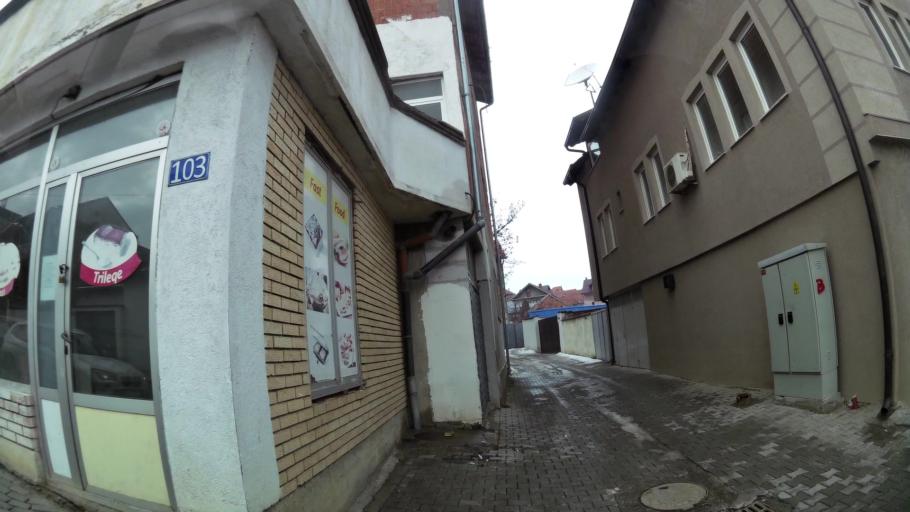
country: XK
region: Pristina
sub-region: Komuna e Prishtines
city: Pristina
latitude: 42.6781
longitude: 21.1665
